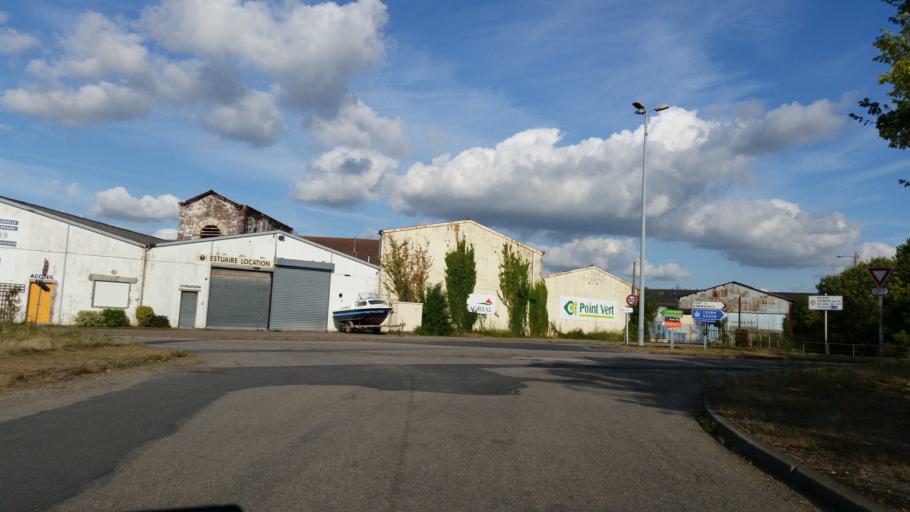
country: FR
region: Lower Normandy
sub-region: Departement du Calvados
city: Honfleur
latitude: 49.4156
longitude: 0.2513
